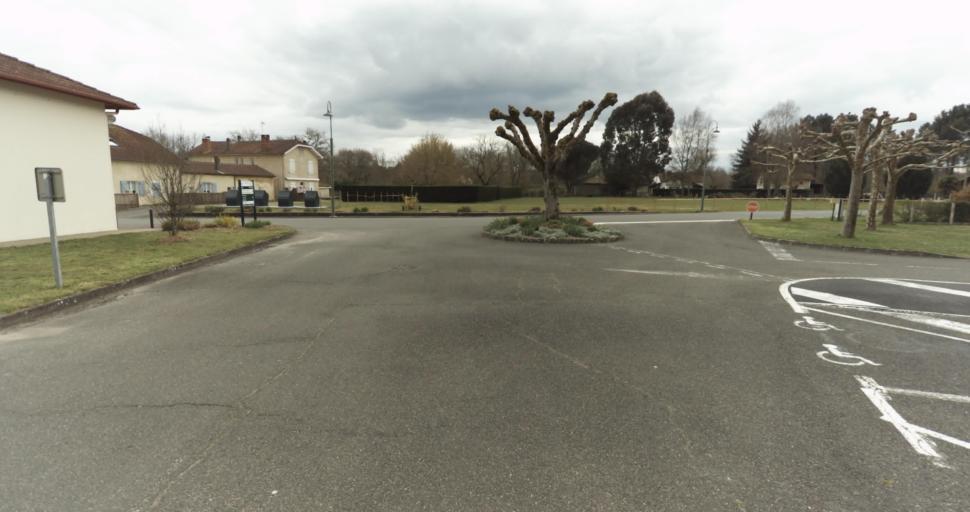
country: FR
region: Aquitaine
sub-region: Departement des Landes
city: Sarbazan
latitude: 44.0188
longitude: -0.3128
